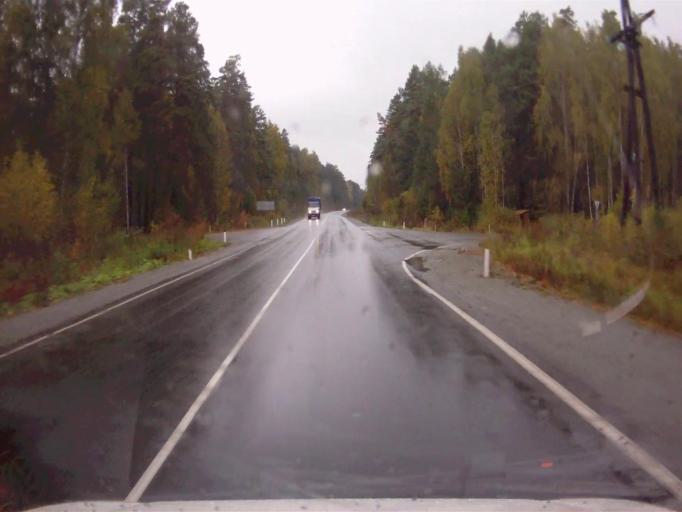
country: RU
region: Chelyabinsk
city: Kyshtym
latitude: 55.6359
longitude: 60.5969
